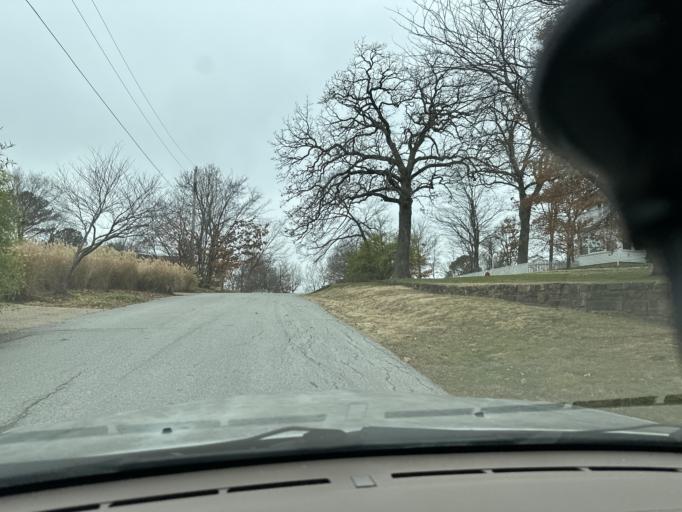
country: US
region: Arkansas
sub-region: Washington County
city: Fayetteville
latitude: 36.0738
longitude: -94.1579
